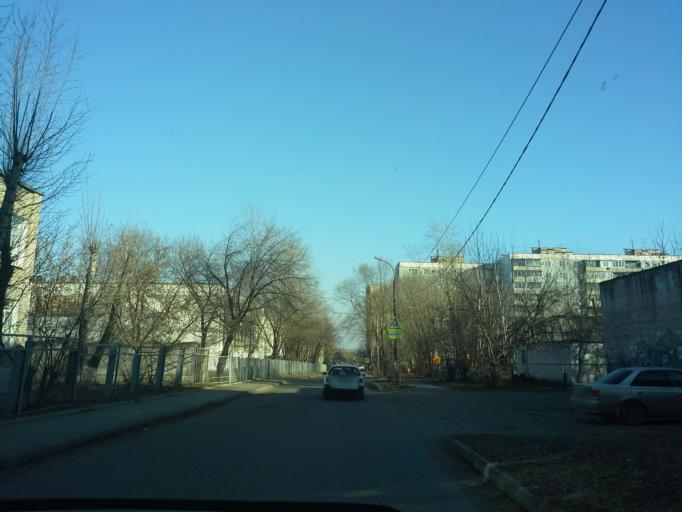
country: RU
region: Khabarovsk Krai
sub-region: Khabarovskiy Rayon
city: Khabarovsk
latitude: 48.4807
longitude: 135.1185
